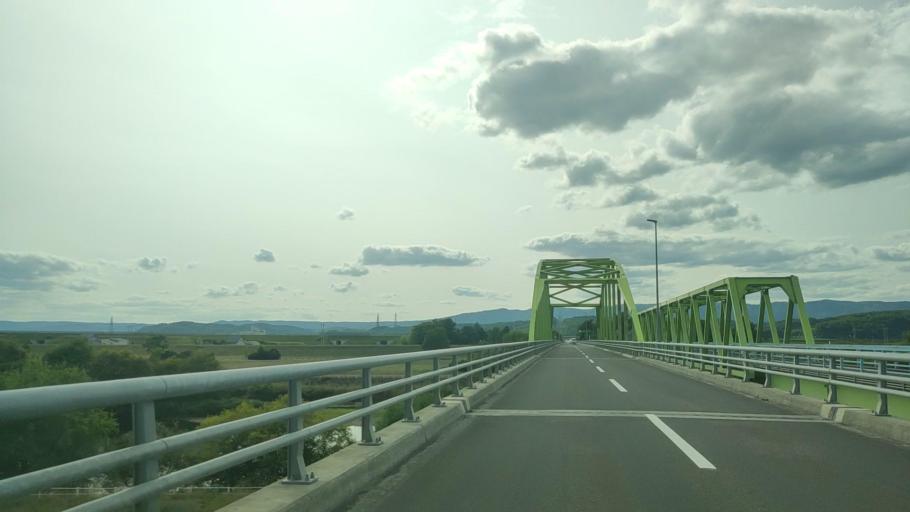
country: JP
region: Hokkaido
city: Nayoro
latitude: 44.3463
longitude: 142.4423
